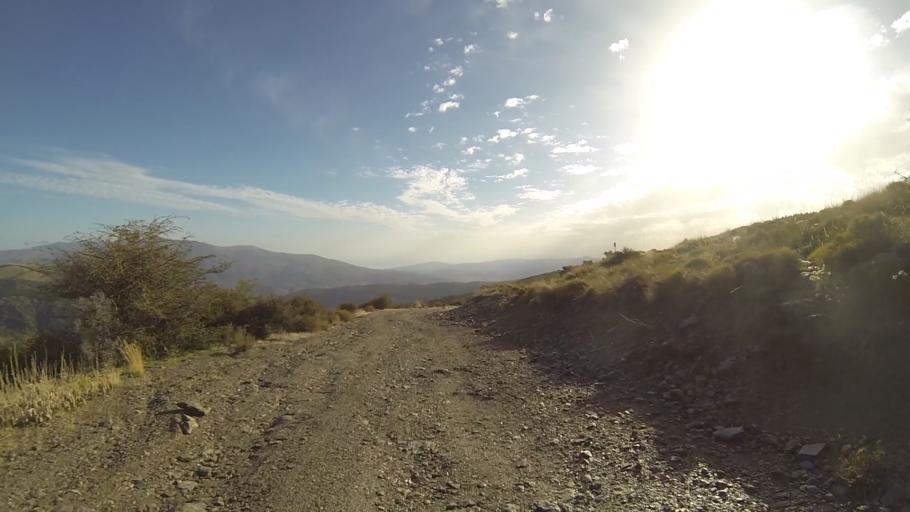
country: ES
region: Andalusia
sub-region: Provincia de Almeria
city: Laujar de Andarax
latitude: 37.0659
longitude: -2.8868
